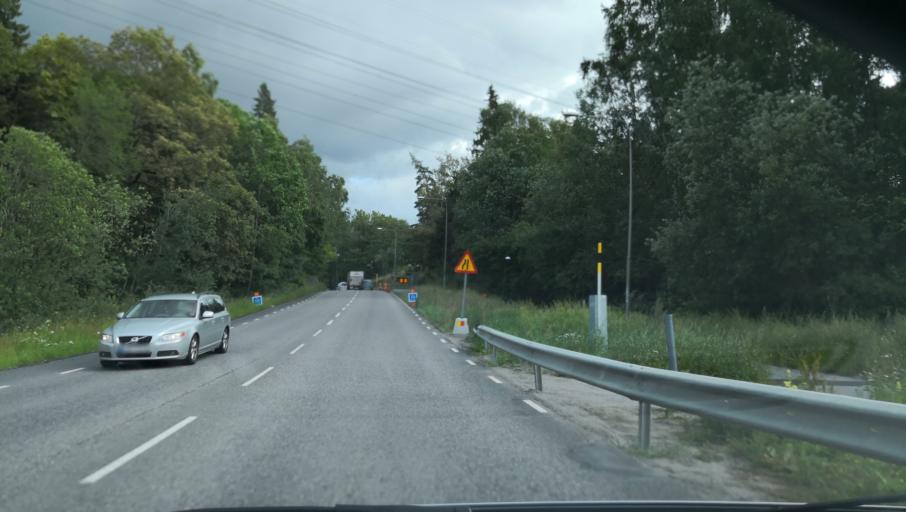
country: SE
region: Stockholm
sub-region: Stockholms Kommun
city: Arsta
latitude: 59.2534
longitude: 18.0487
